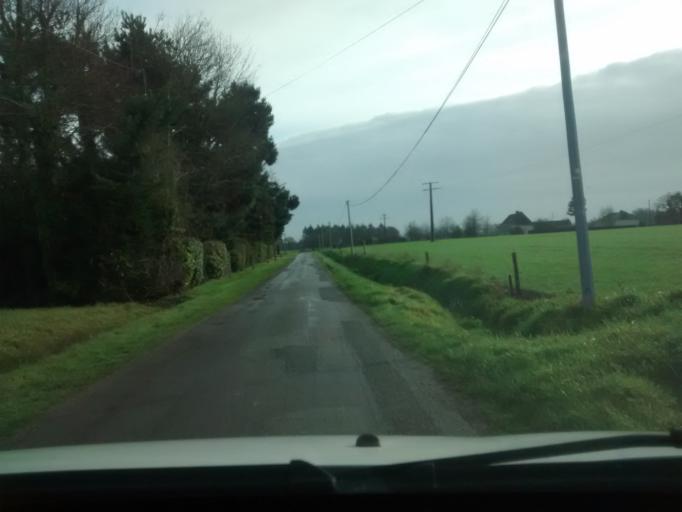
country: FR
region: Brittany
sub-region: Departement d'Ille-et-Vilaine
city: Pace
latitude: 48.1426
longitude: -1.7569
